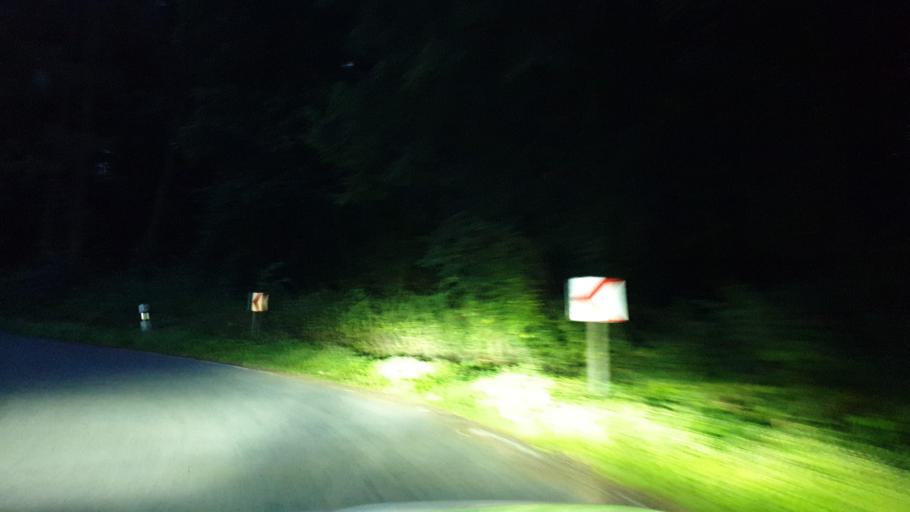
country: DE
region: North Rhine-Westphalia
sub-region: Regierungsbezirk Detmold
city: Huellhorst
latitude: 52.2909
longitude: 8.7094
